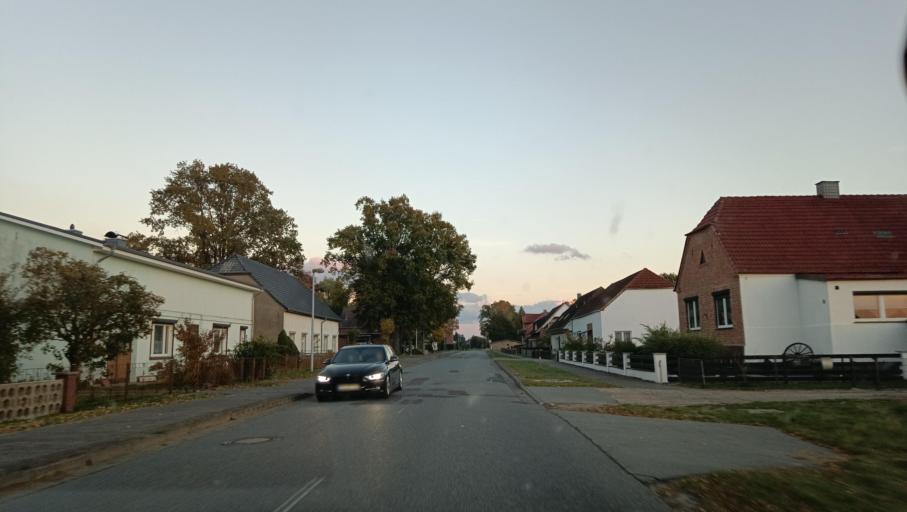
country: DE
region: Mecklenburg-Vorpommern
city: Ludwigslust
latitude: 53.2832
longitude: 11.4840
